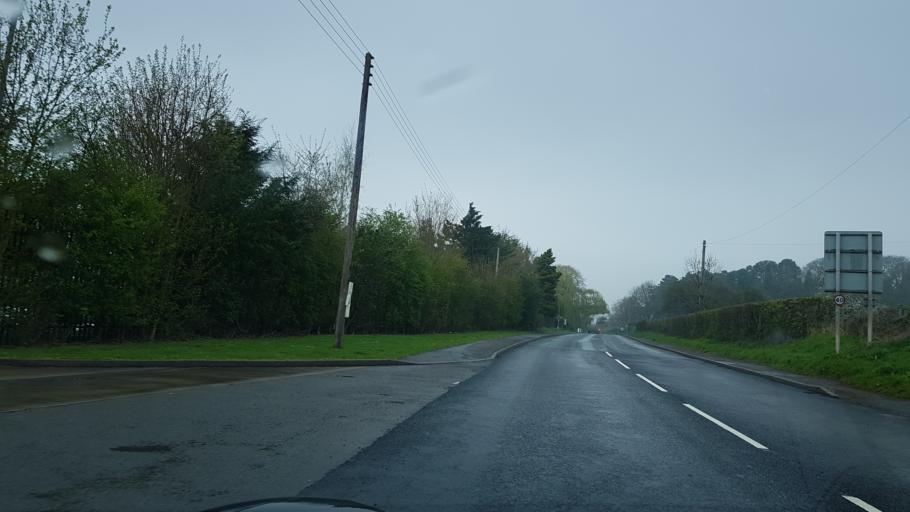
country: GB
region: England
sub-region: Herefordshire
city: Ledbury
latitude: 52.0469
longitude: -2.4270
